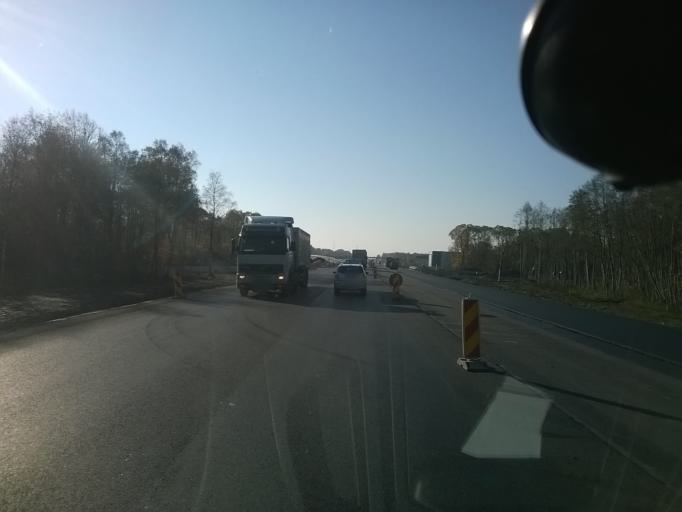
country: EE
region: Harju
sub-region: Rae vald
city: Jueri
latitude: 59.3780
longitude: 24.9155
